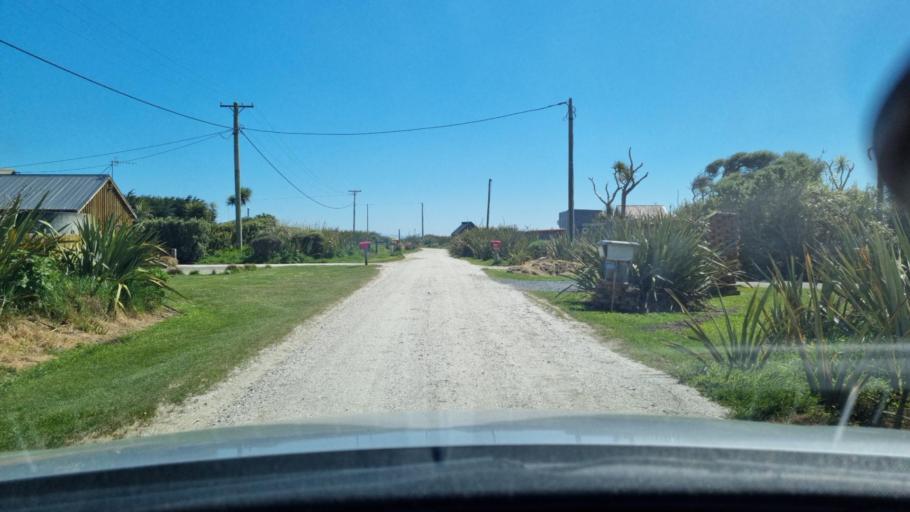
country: NZ
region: Southland
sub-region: Invercargill City
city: Invercargill
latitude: -46.4301
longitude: 168.2323
